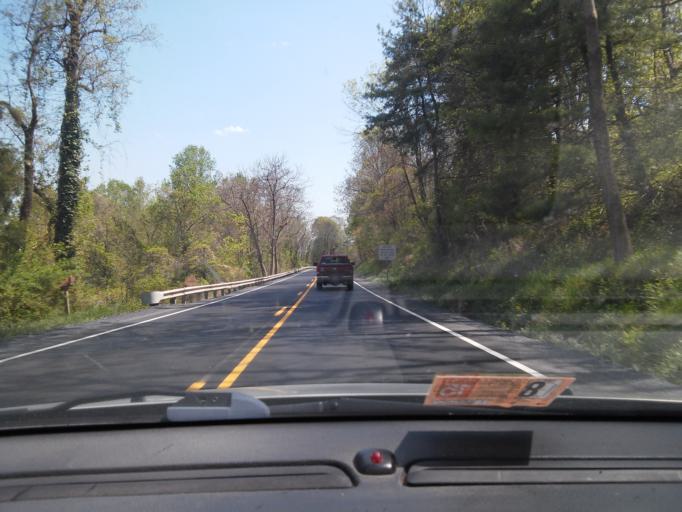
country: US
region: Virginia
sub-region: Warren County
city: Apple Mountain Lake
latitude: 38.8575
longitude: -78.1293
